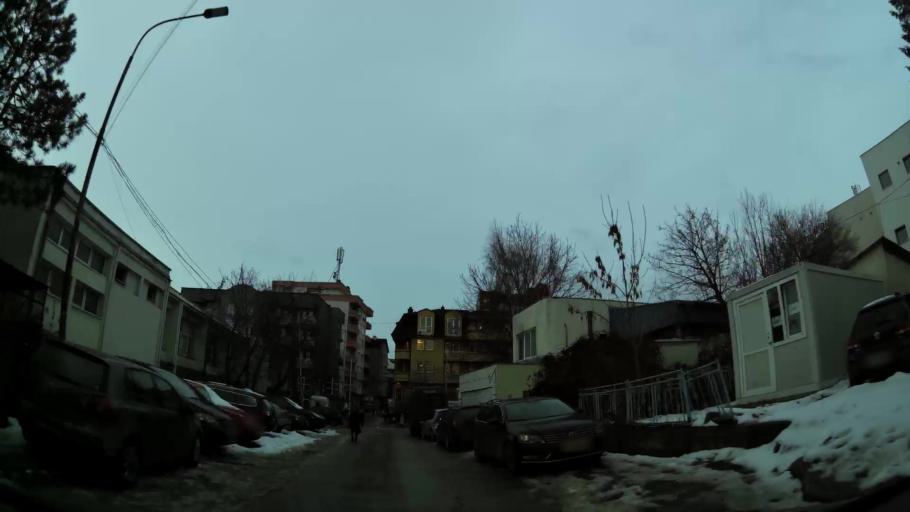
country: XK
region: Pristina
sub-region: Komuna e Prishtines
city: Pristina
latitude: 42.6594
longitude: 21.1674
